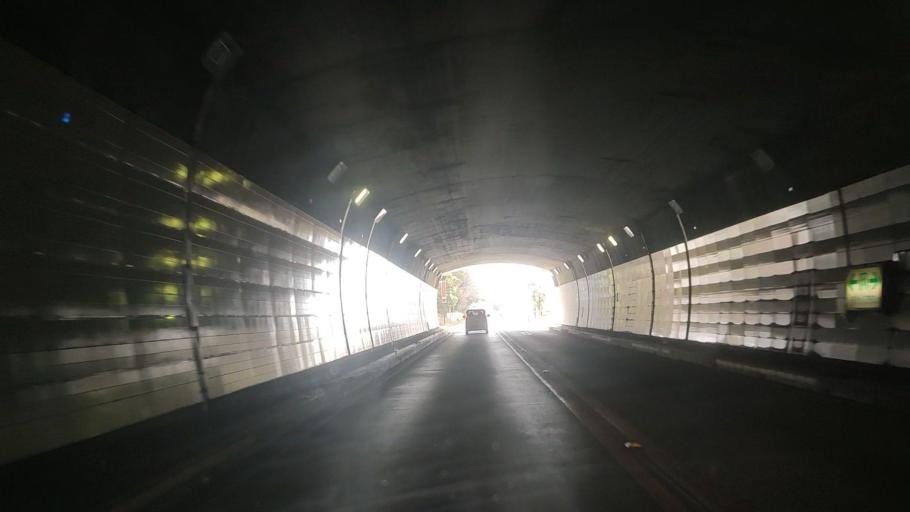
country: JP
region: Kumamoto
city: Hitoyoshi
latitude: 32.0894
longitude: 130.8017
